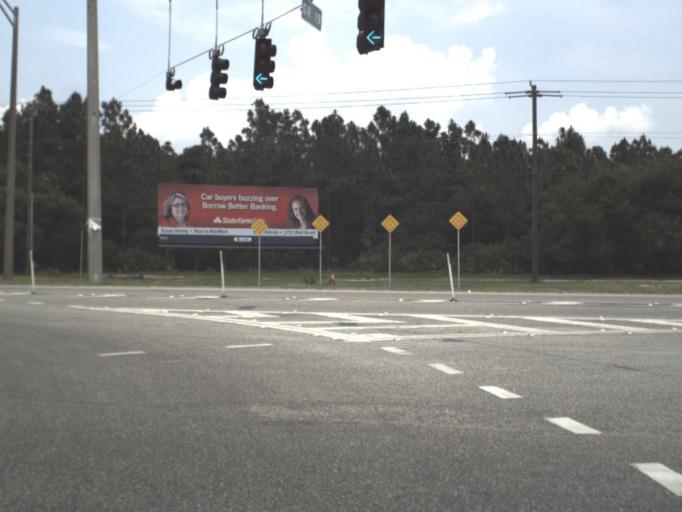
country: US
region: Florida
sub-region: Putnam County
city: Palatka
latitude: 29.6684
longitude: -81.6569
